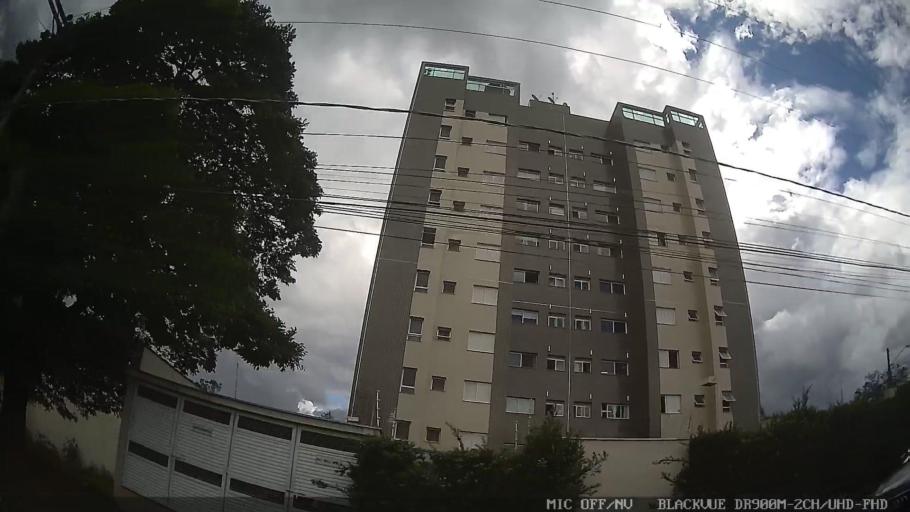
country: BR
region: Sao Paulo
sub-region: Jaguariuna
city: Jaguariuna
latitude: -22.7086
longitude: -46.9907
